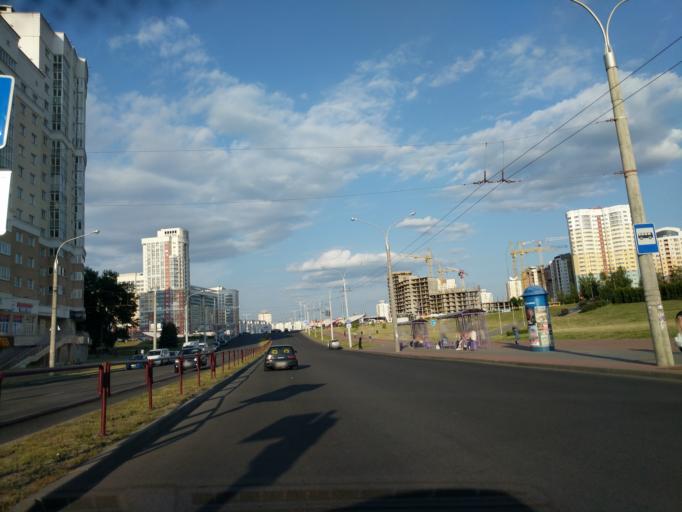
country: BY
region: Minsk
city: Shchomyslitsa
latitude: 53.8491
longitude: 27.4701
